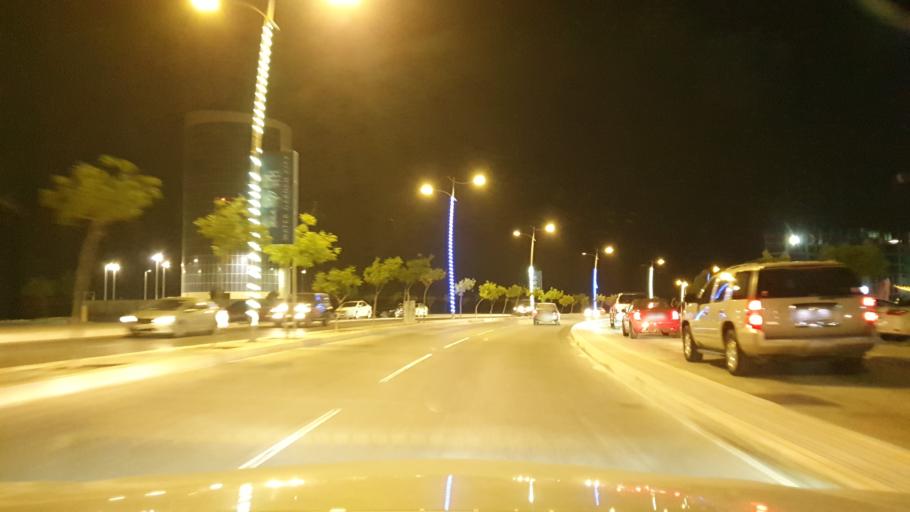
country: BH
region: Manama
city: Jidd Hafs
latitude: 26.2412
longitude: 50.5525
